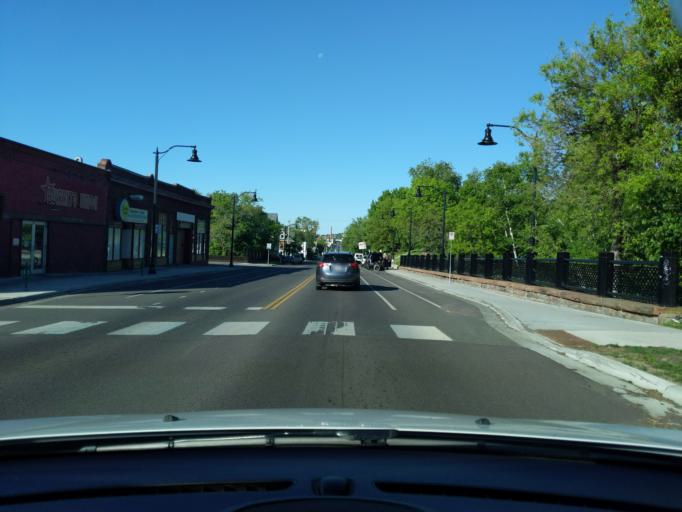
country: US
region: Minnesota
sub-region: Saint Louis County
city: Duluth
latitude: 46.8030
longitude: -92.0851
